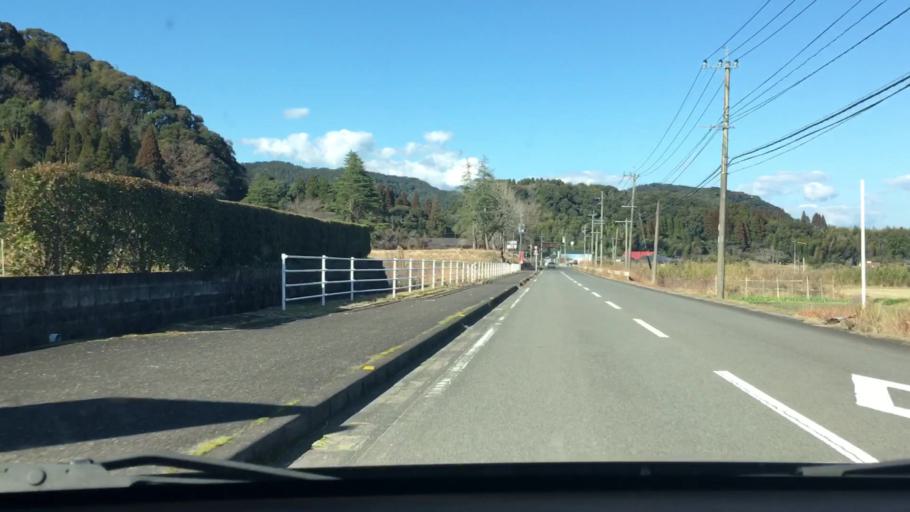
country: JP
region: Kagoshima
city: Satsumasendai
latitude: 31.7754
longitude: 130.4010
